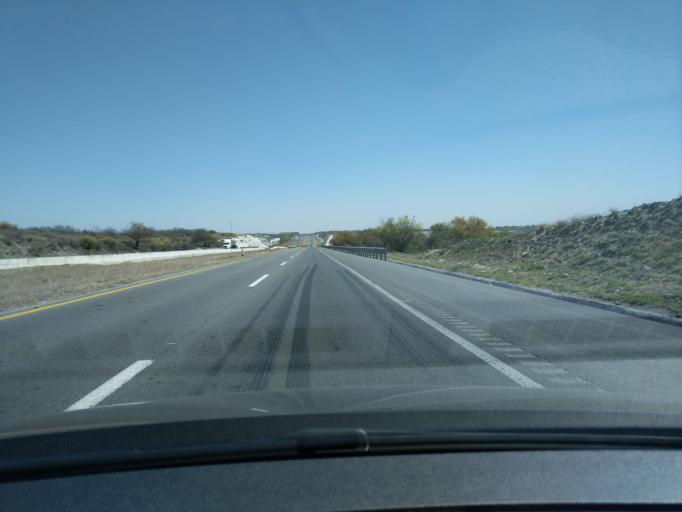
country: MX
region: Nuevo Leon
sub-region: Apodaca
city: Loma la Paz
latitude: 25.6939
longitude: -100.0977
